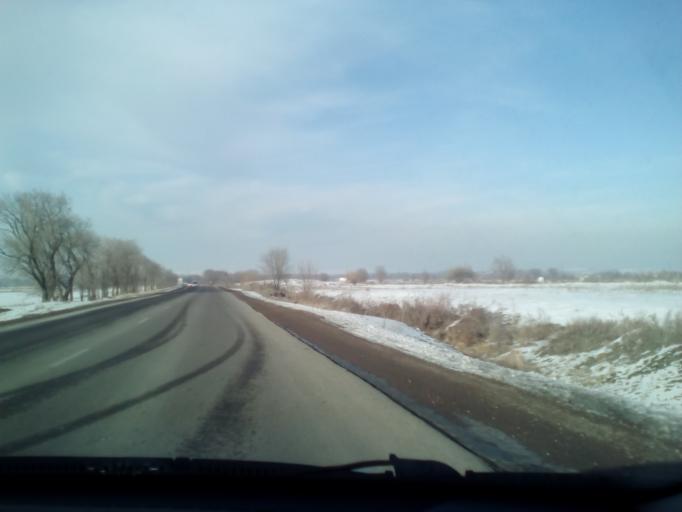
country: KZ
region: Almaty Oblysy
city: Burunday
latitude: 43.2061
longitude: 76.4150
